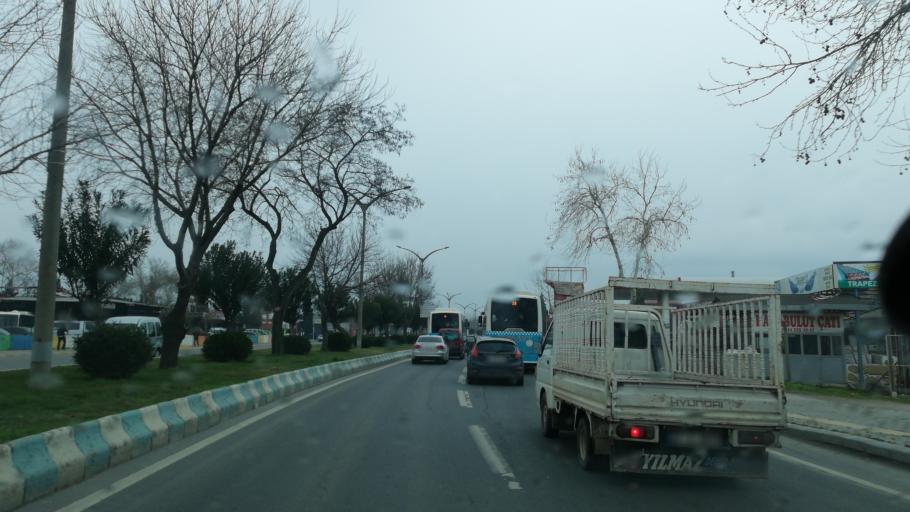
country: TR
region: Kahramanmaras
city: Kahramanmaras
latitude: 37.5620
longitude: 36.9541
